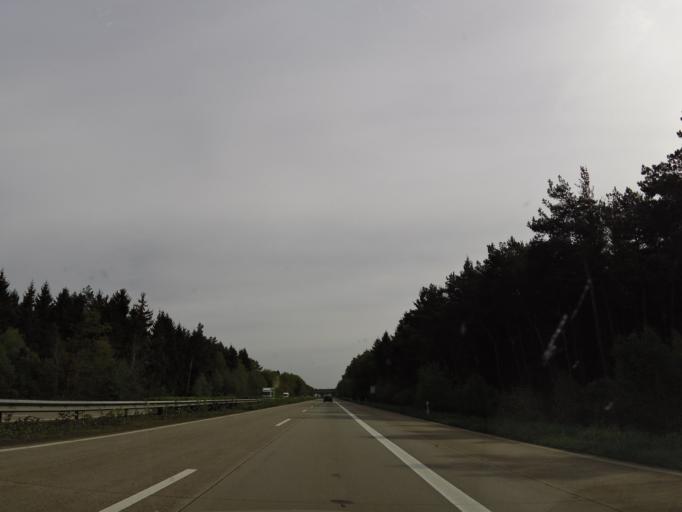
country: DE
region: Lower Saxony
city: Soltau
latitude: 52.9706
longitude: 9.9117
